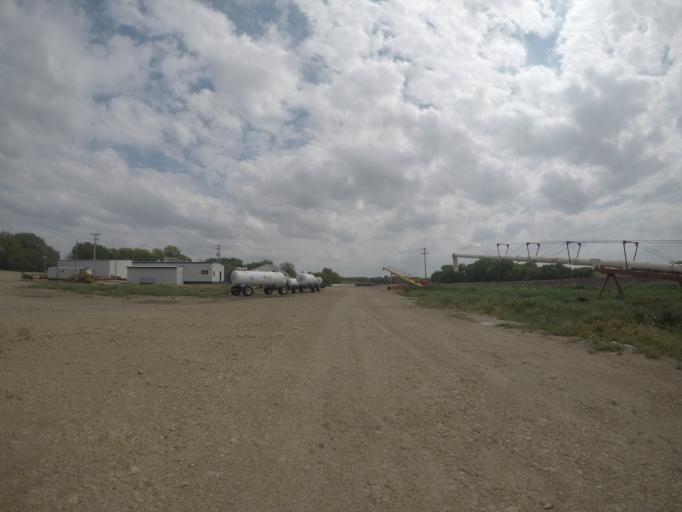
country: US
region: Kansas
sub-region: Marshall County
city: Marysville
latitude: 39.9440
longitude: -96.6101
